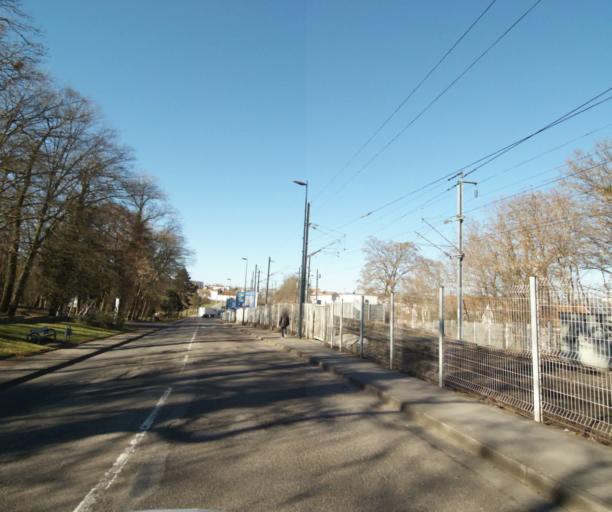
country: FR
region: Lorraine
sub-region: Departement de Meurthe-et-Moselle
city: Jarville-la-Malgrange
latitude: 48.6675
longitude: 6.2079
